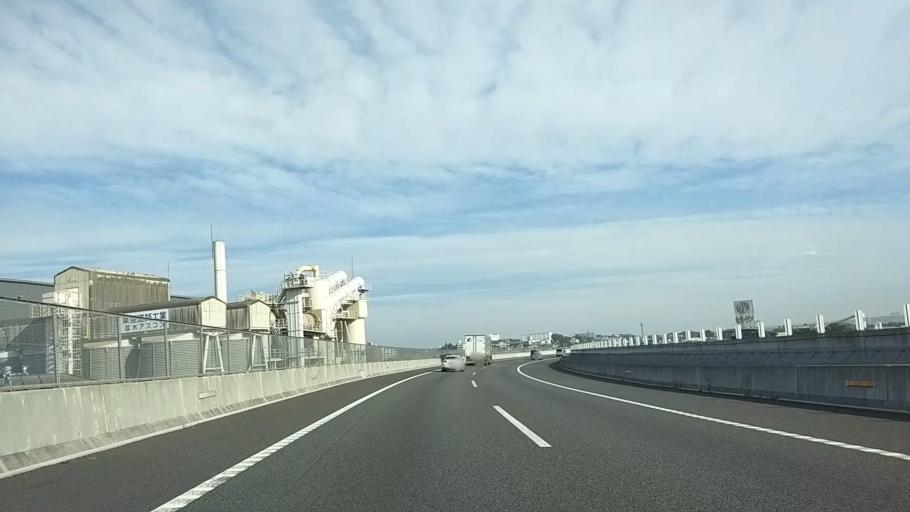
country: JP
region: Kanagawa
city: Atsugi
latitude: 35.4561
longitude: 139.3726
